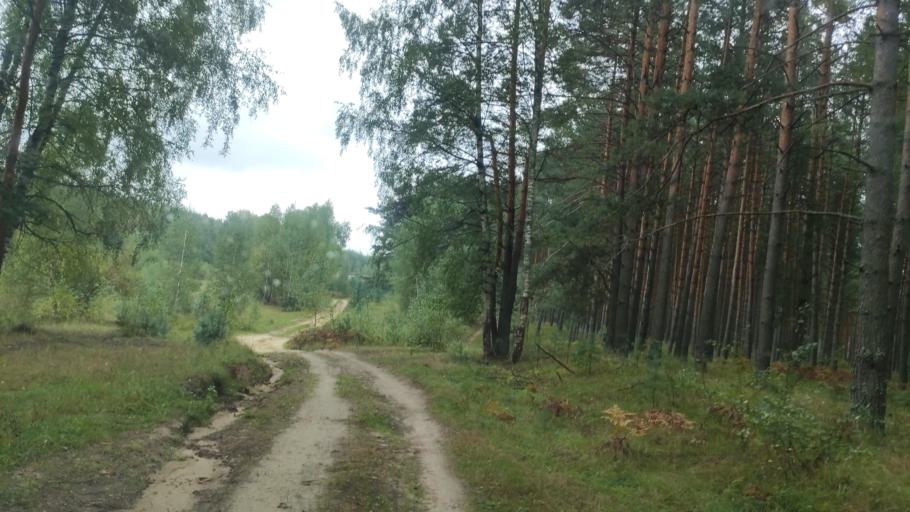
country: RU
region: Nizjnij Novgorod
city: Taremskoye
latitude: 55.9975
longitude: 42.9837
